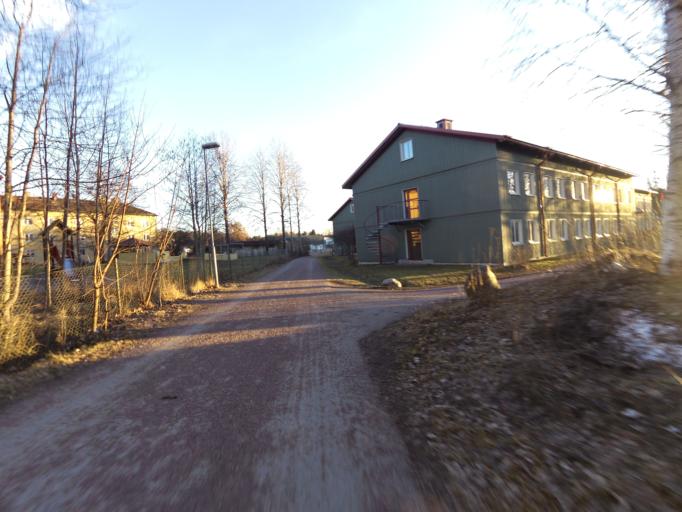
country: SE
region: Gaevleborg
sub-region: Gavle Kommun
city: Gavle
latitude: 60.6675
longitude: 17.1223
